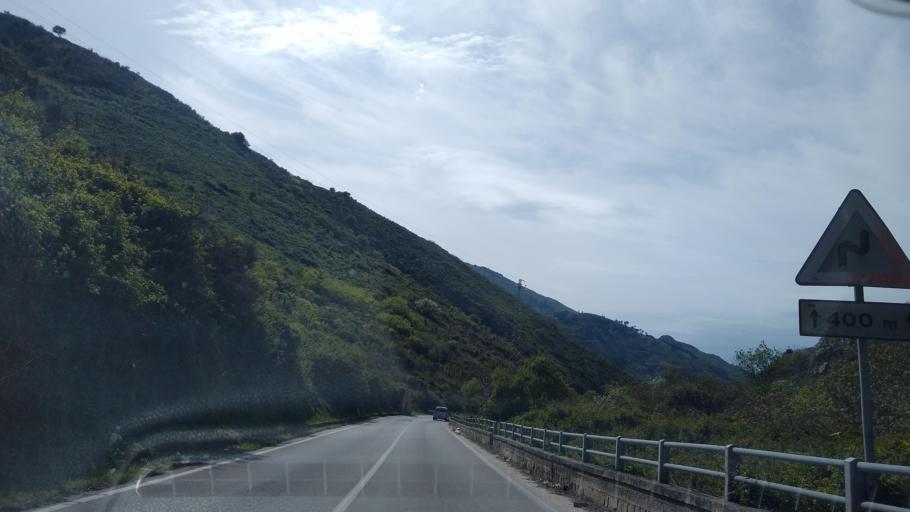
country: IT
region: Sicily
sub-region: Palermo
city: Pioppo
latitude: 38.0487
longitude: 13.1972
